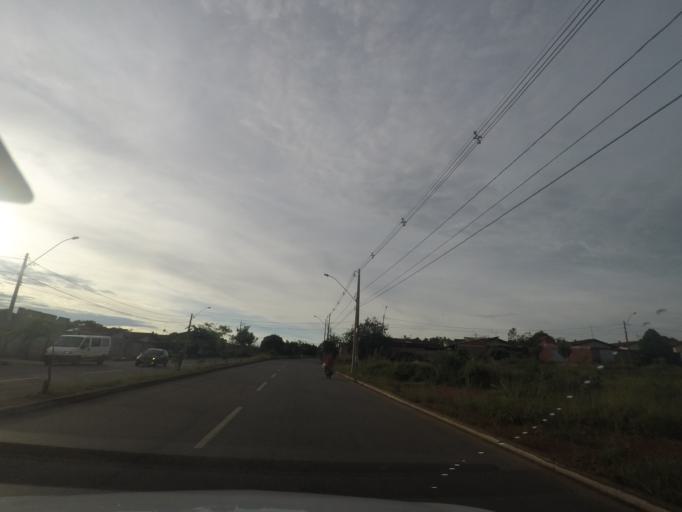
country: BR
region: Goias
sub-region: Trindade
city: Trindade
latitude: -16.7305
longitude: -49.4011
